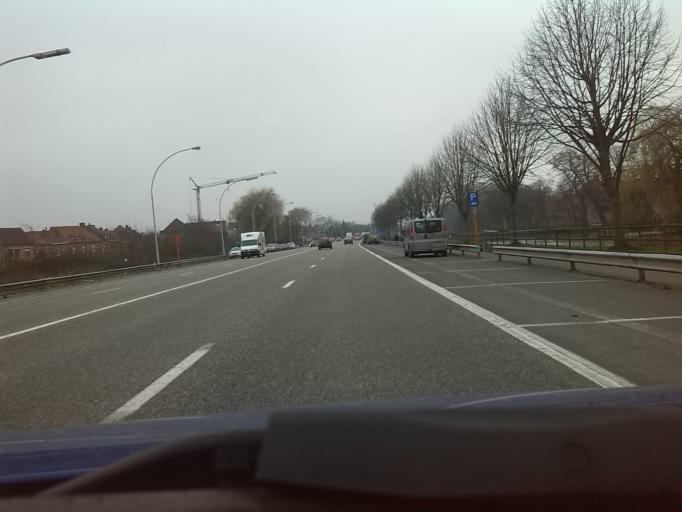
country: BE
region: Flanders
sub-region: Provincie West-Vlaanderen
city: Sint-Kruis
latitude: 51.2052
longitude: 3.2382
